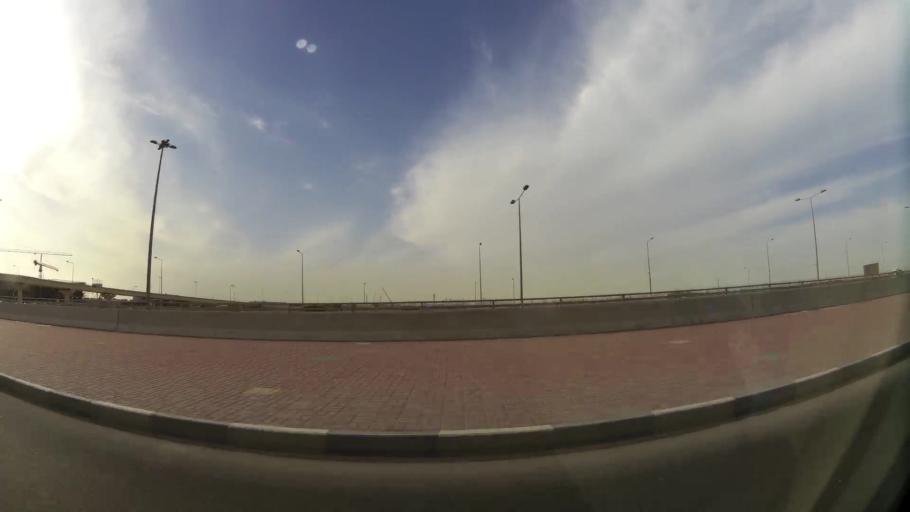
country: QA
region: Al Wakrah
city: Al Wakrah
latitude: 25.2321
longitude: 51.5785
